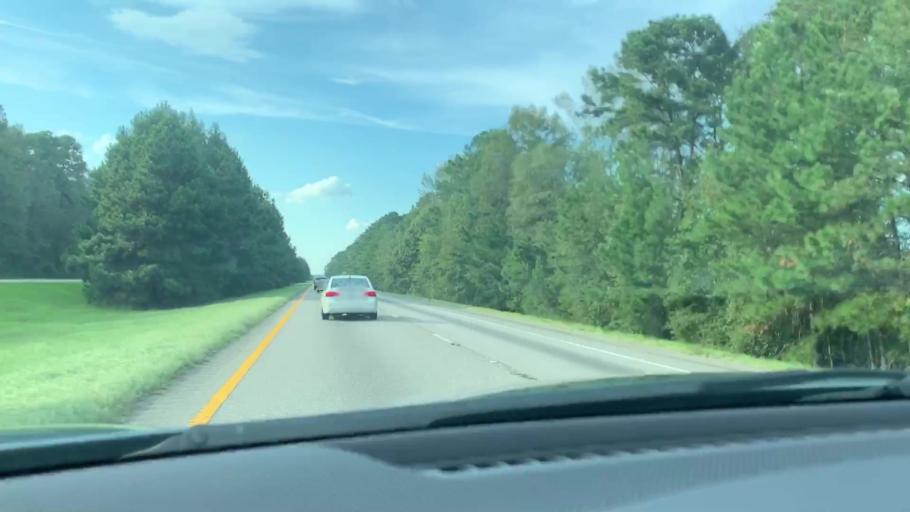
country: US
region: South Carolina
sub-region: Orangeburg County
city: Brookdale
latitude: 33.4350
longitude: -80.6983
